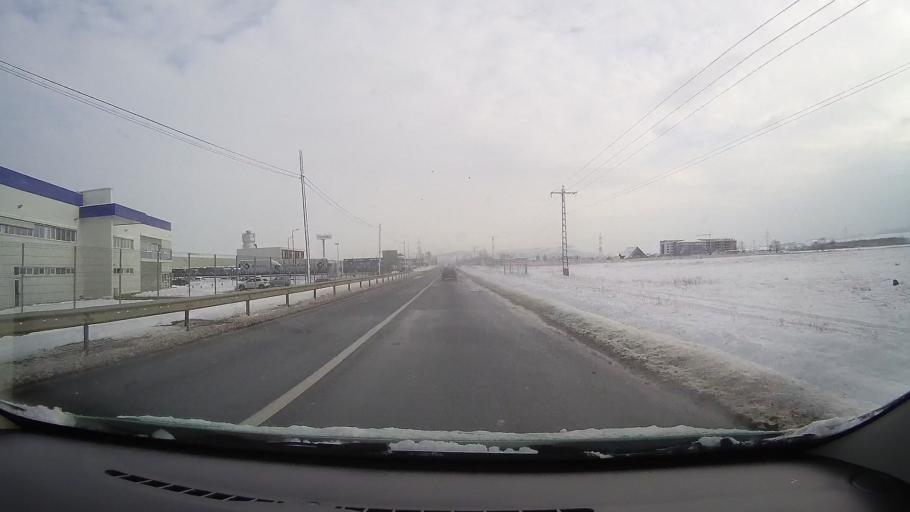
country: RO
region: Alba
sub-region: Municipiul Sebes
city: Sebes
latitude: 45.9597
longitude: 23.5444
